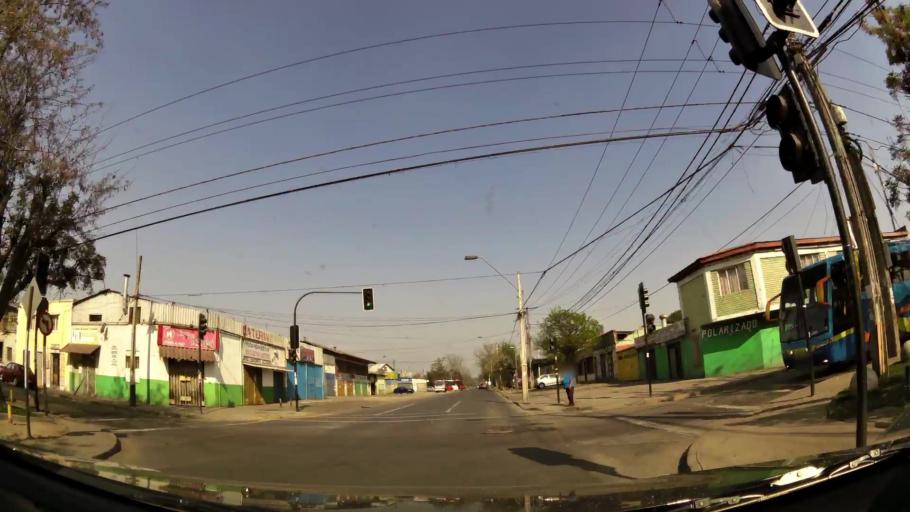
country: CL
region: Santiago Metropolitan
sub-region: Provincia de Santiago
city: Santiago
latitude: -33.3794
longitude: -70.6721
